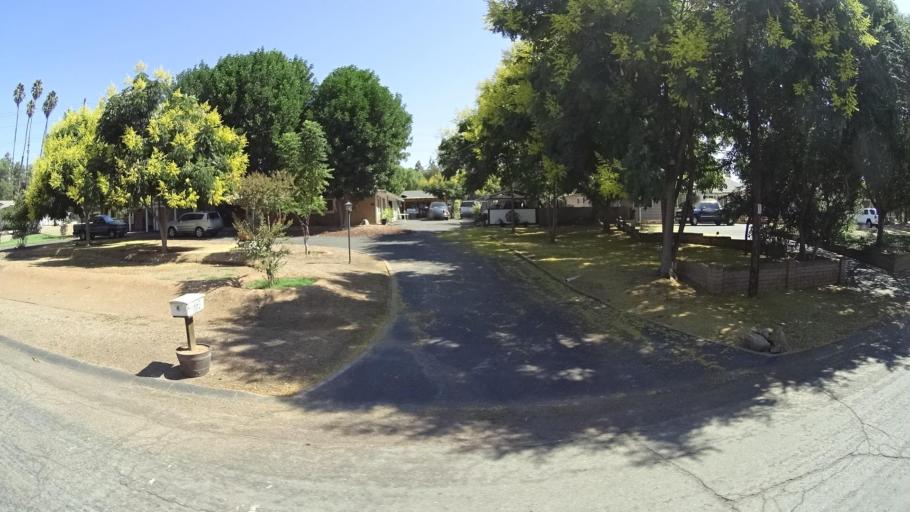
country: US
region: California
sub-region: San Diego County
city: Granite Hills
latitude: 32.8019
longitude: -116.9121
